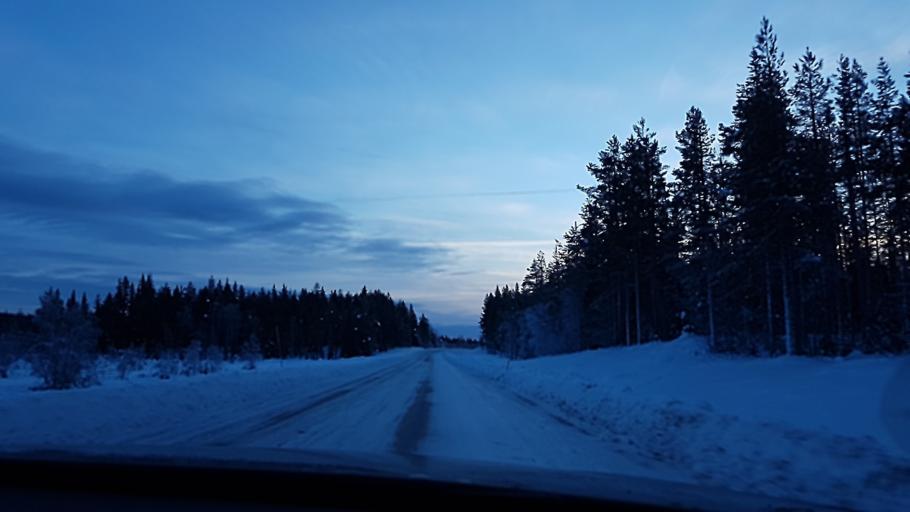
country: SE
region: Norrbotten
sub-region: Jokkmokks Kommun
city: Jokkmokk
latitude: 66.1124
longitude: 20.0448
